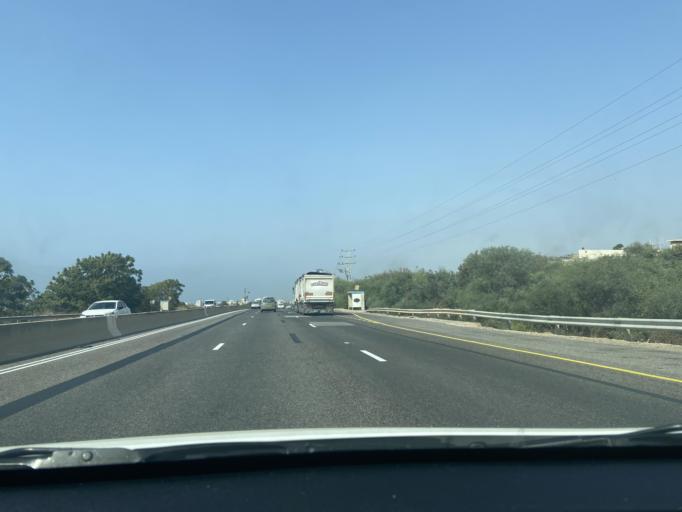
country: IL
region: Northern District
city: El Mazra`a
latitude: 32.9693
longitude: 35.0930
